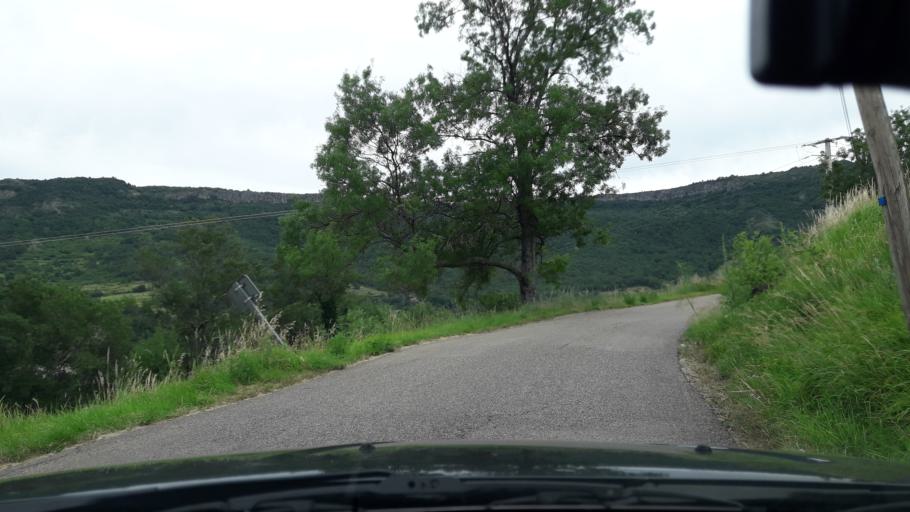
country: FR
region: Rhone-Alpes
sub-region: Departement de l'Ardeche
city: Alissas
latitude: 44.6870
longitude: 4.6327
